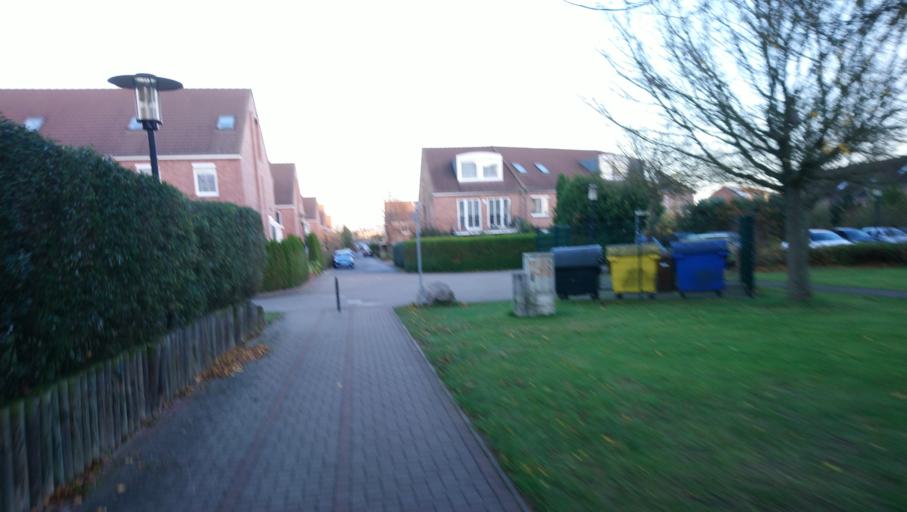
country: DE
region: Mecklenburg-Vorpommern
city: Papendorf
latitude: 54.0615
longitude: 12.1134
